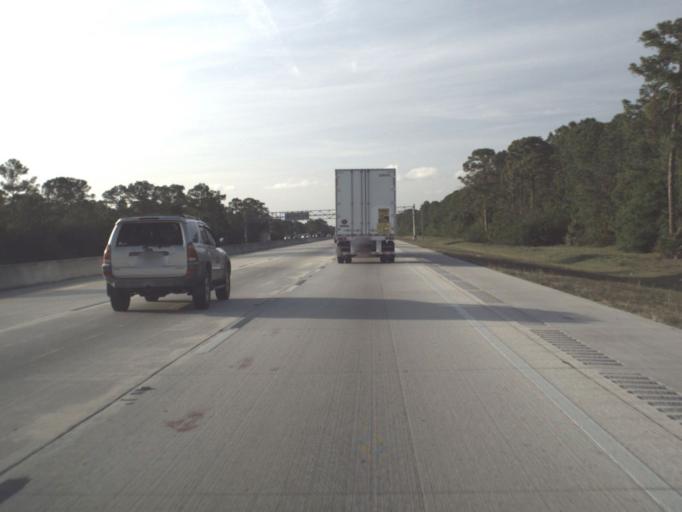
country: US
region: Florida
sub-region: Brevard County
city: Cocoa West
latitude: 28.3916
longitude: -80.8148
